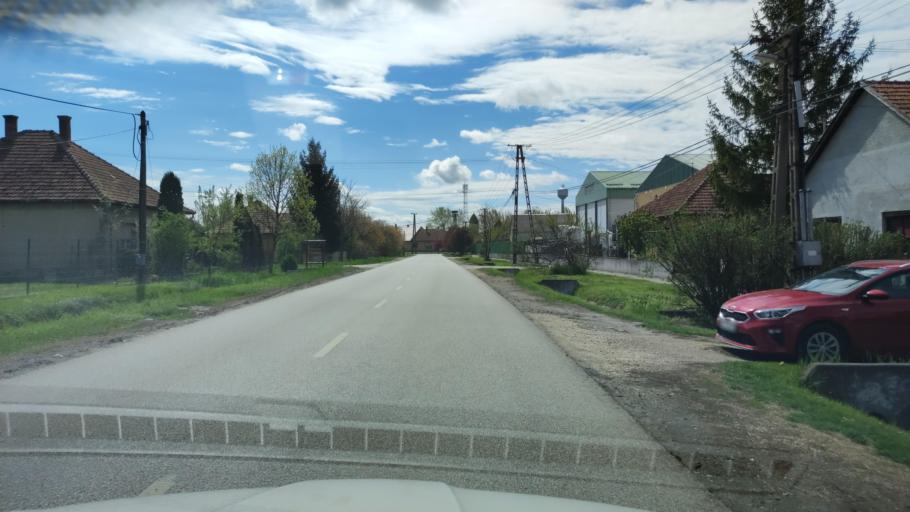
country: HU
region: Pest
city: Jaszkarajeno
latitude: 47.1008
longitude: 20.0211
